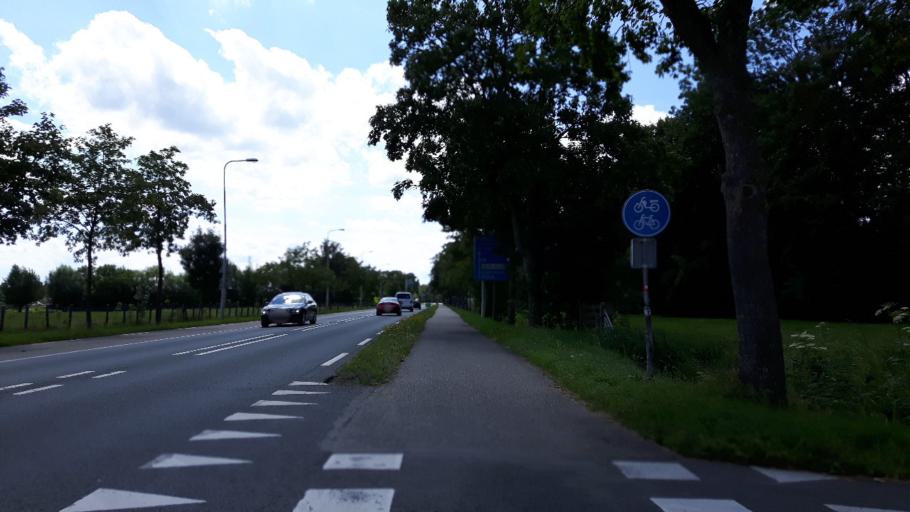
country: NL
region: Utrecht
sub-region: Stichtse Vecht
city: Vreeland
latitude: 52.2228
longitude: 5.0121
